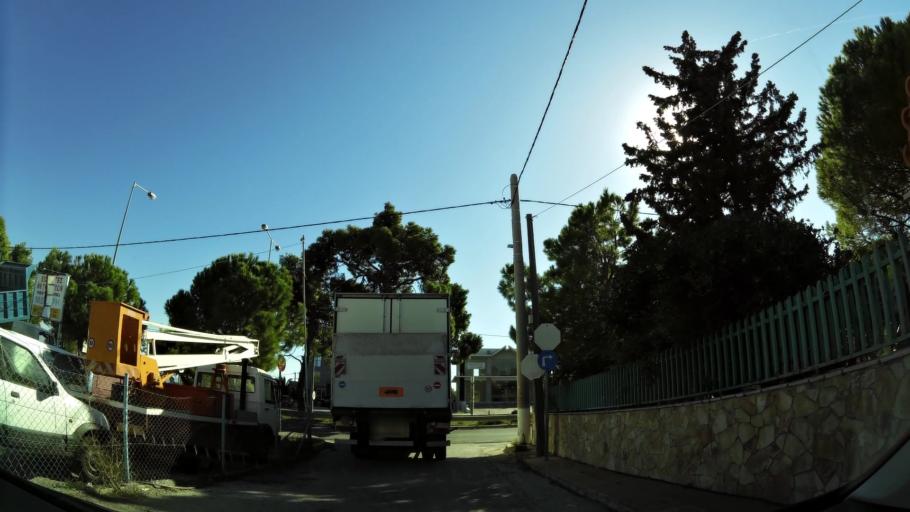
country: GR
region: Attica
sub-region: Nomarchia Anatolikis Attikis
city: Dhrafi
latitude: 38.0028
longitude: 23.9054
